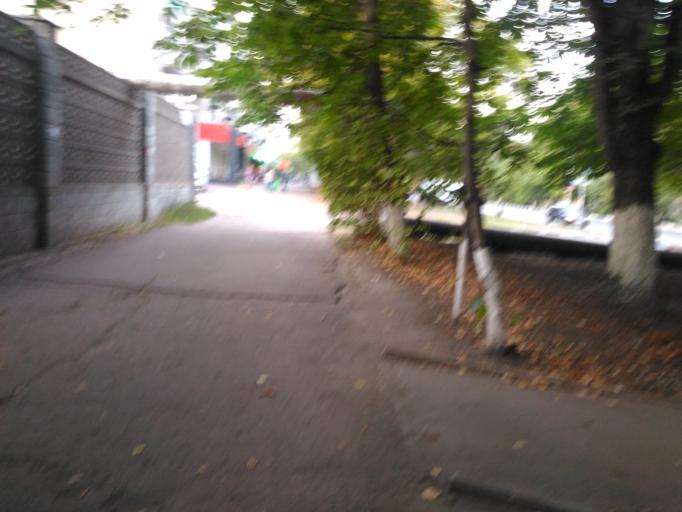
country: RU
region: Ulyanovsk
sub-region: Ulyanovskiy Rayon
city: Ulyanovsk
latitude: 54.2999
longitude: 48.3296
